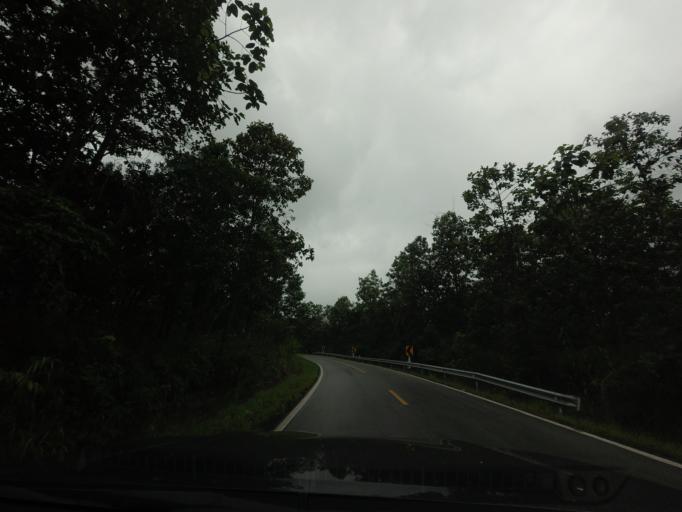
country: TH
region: Nong Khai
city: Sangkhom
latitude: 18.0298
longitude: 102.3422
